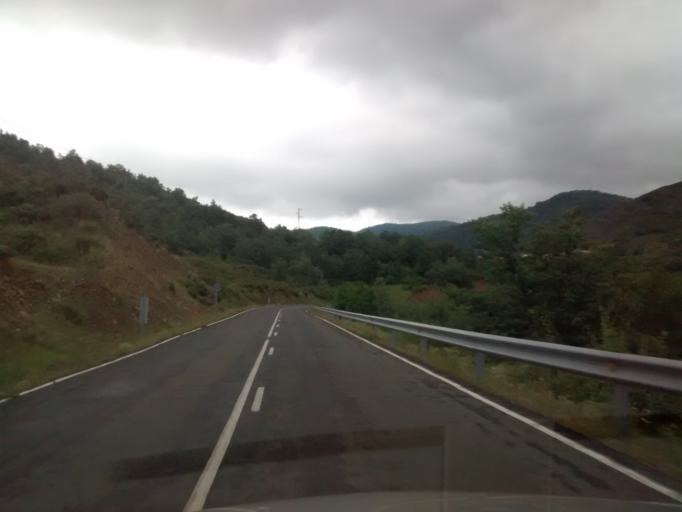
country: ES
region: La Rioja
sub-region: Provincia de La Rioja
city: Rabanera
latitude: 42.1953
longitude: -2.4804
